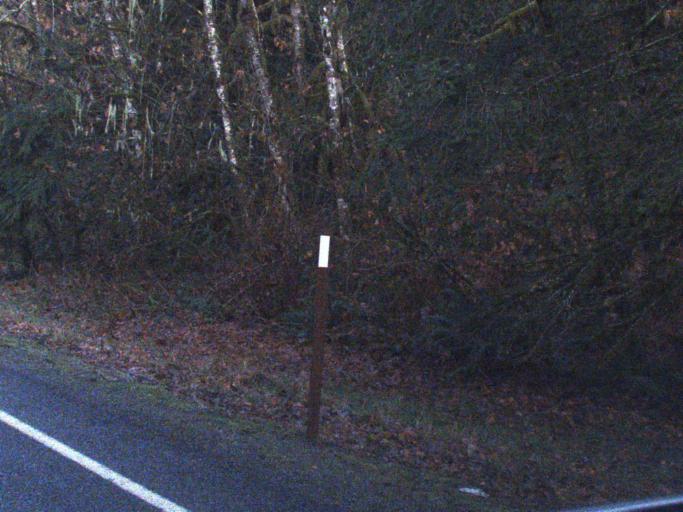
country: US
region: Washington
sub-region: Snohomish County
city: Darrington
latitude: 48.3907
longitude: -121.5500
